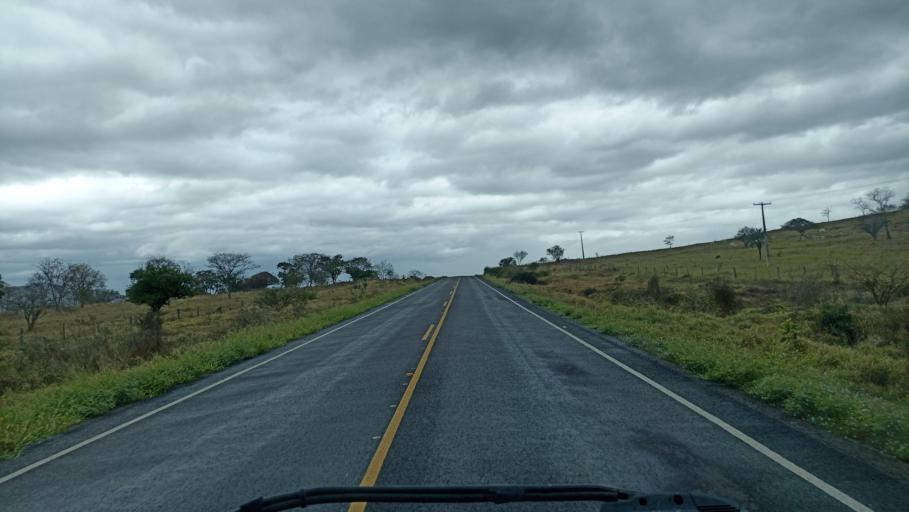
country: BR
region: Bahia
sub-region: Iacu
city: Iacu
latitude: -12.9662
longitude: -40.4902
